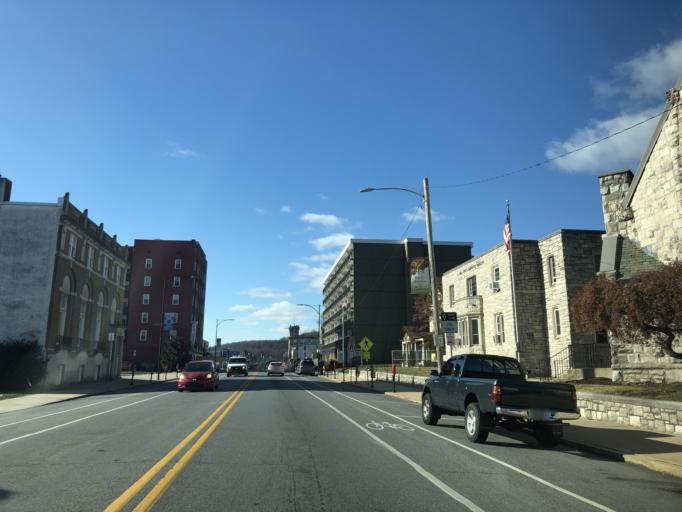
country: US
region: Pennsylvania
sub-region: Chester County
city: Coatesville
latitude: 39.9841
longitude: -75.8174
